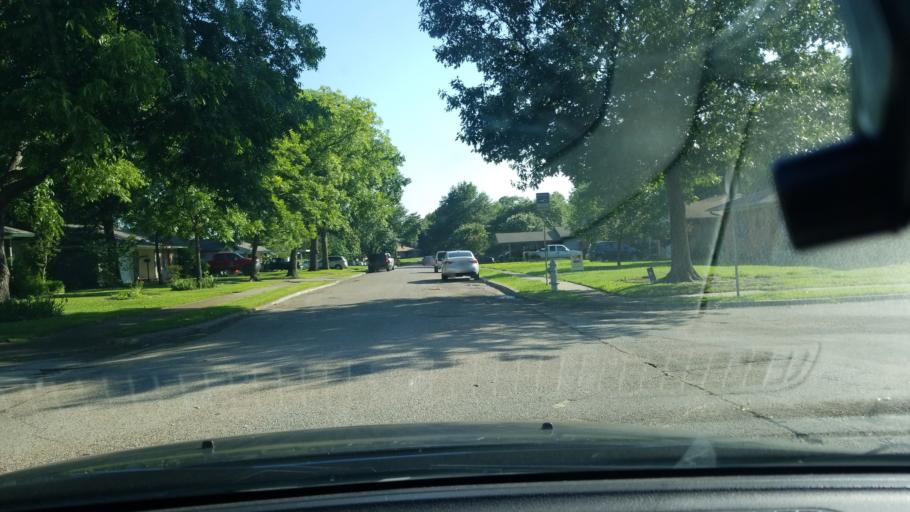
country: US
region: Texas
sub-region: Dallas County
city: Mesquite
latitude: 32.7531
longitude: -96.5979
